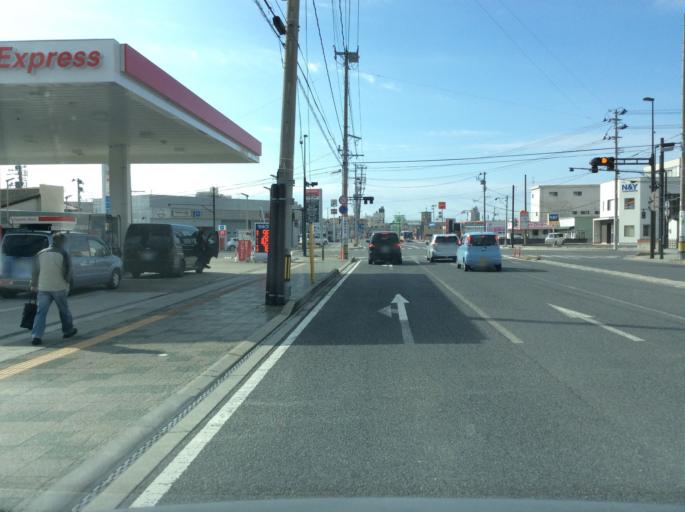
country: JP
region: Fukushima
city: Iwaki
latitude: 36.9585
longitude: 140.9038
